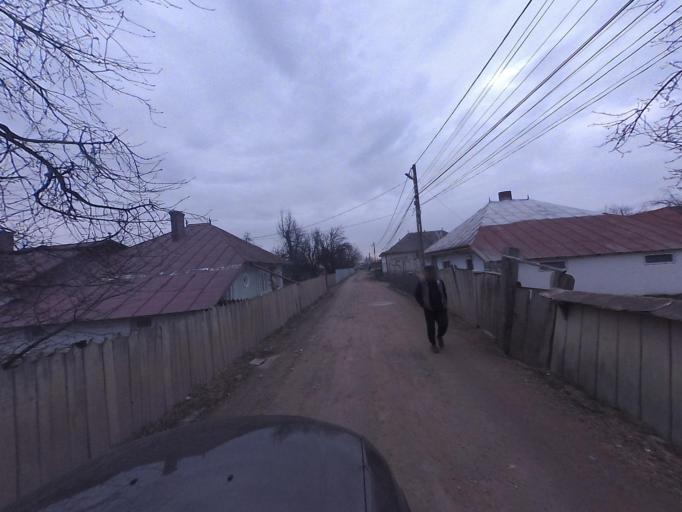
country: RO
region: Neamt
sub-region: Oras Targu Neamt
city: Humulesti
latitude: 47.1949
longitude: 26.3446
